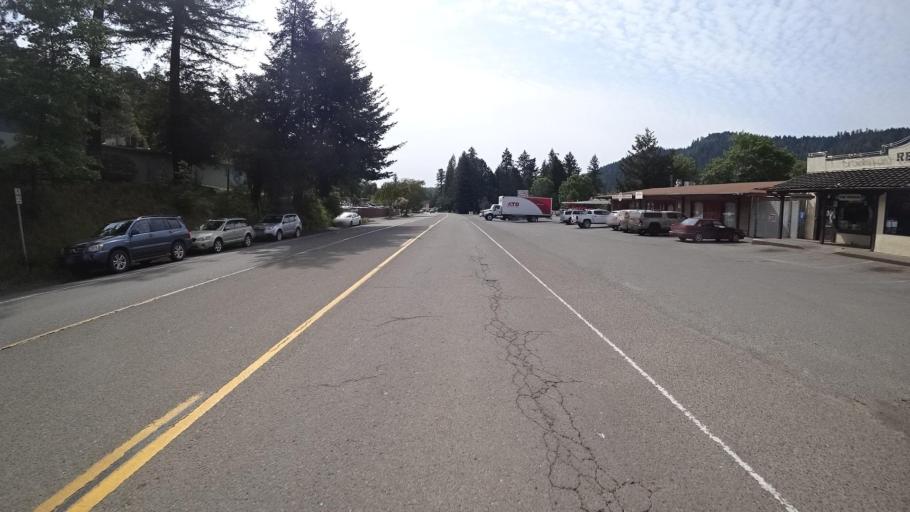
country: US
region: California
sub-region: Humboldt County
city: Redway
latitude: 40.1197
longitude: -123.8226
